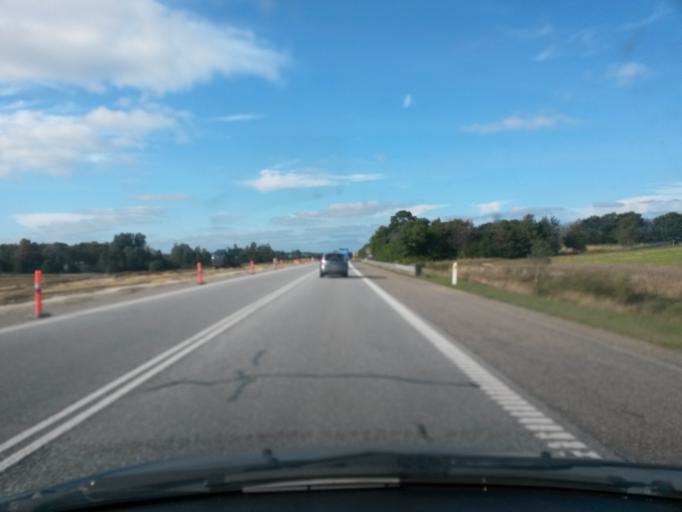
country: DK
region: Central Jutland
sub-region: Herning Kommune
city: Snejbjerg
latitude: 56.1998
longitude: 8.8793
